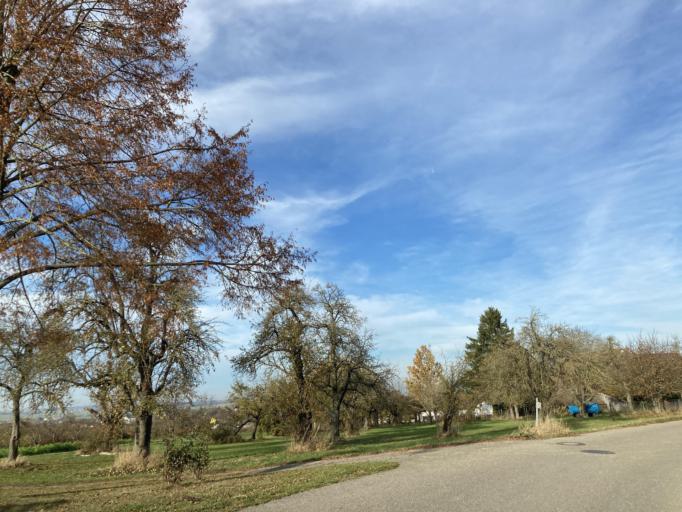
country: DE
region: Baden-Wuerttemberg
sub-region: Regierungsbezirk Stuttgart
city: Bondorf
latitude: 48.4711
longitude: 8.8146
